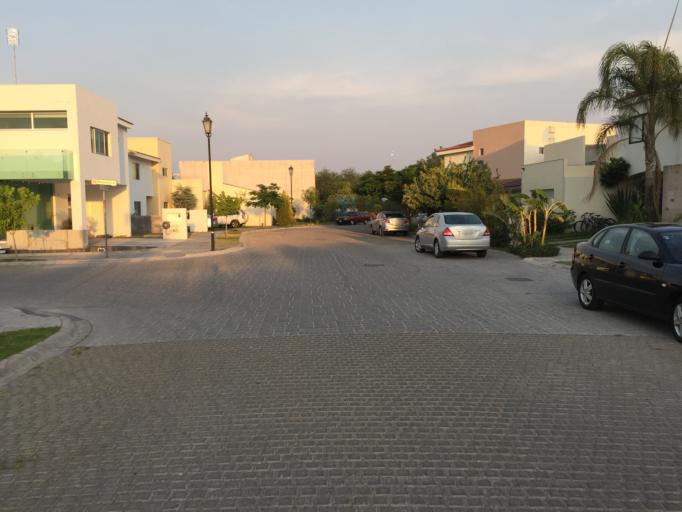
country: MX
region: Aguascalientes
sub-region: Aguascalientes
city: La Loma de los Negritos
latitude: 21.8478
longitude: -102.3570
